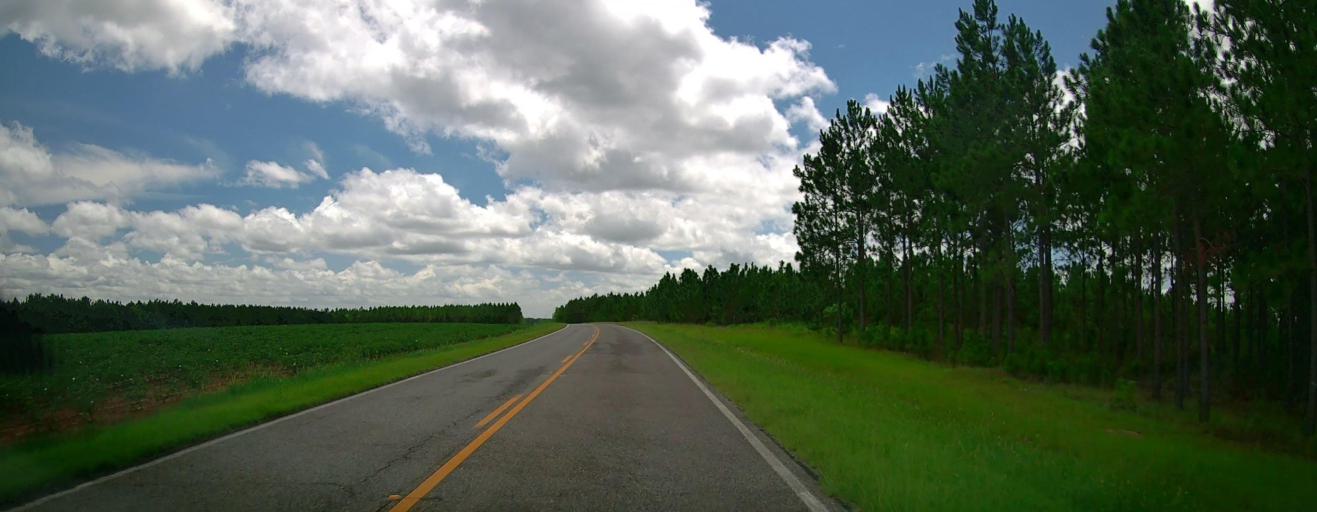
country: US
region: Georgia
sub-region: Wilcox County
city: Rochelle
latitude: 31.8763
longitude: -83.5582
